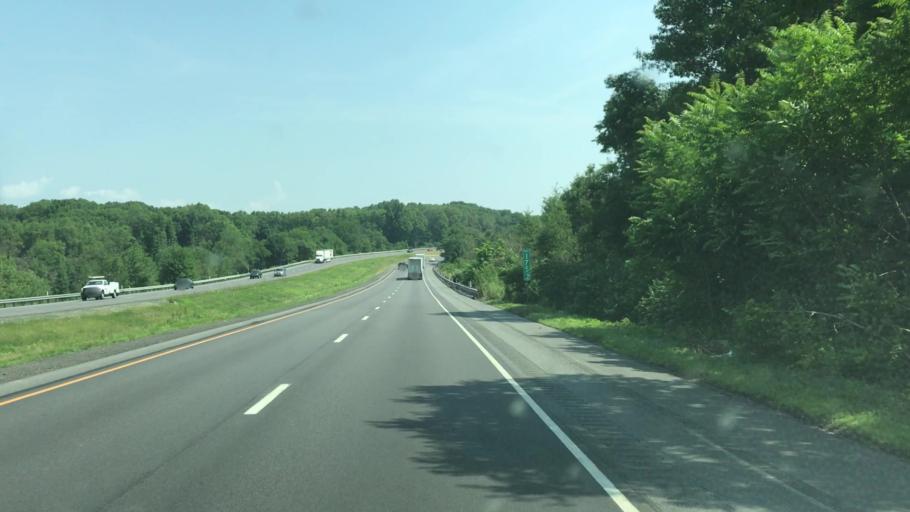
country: US
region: Pennsylvania
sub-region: Luzerne County
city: Hughestown
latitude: 41.3075
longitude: -75.7648
